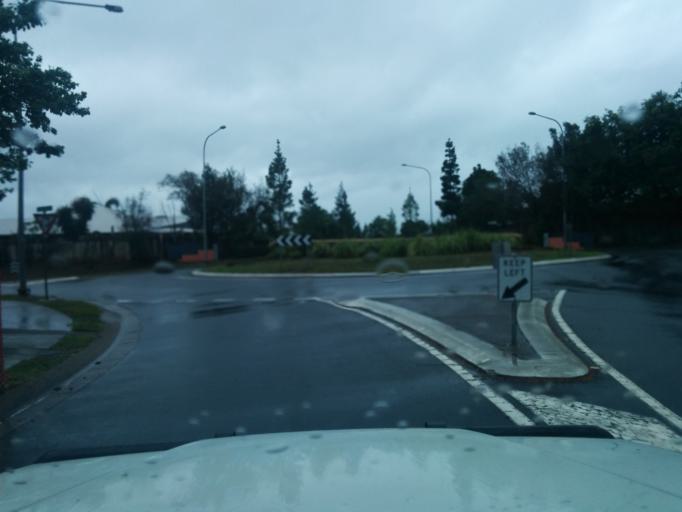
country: AU
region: Queensland
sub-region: Cairns
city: Woree
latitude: -16.9833
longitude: 145.7369
